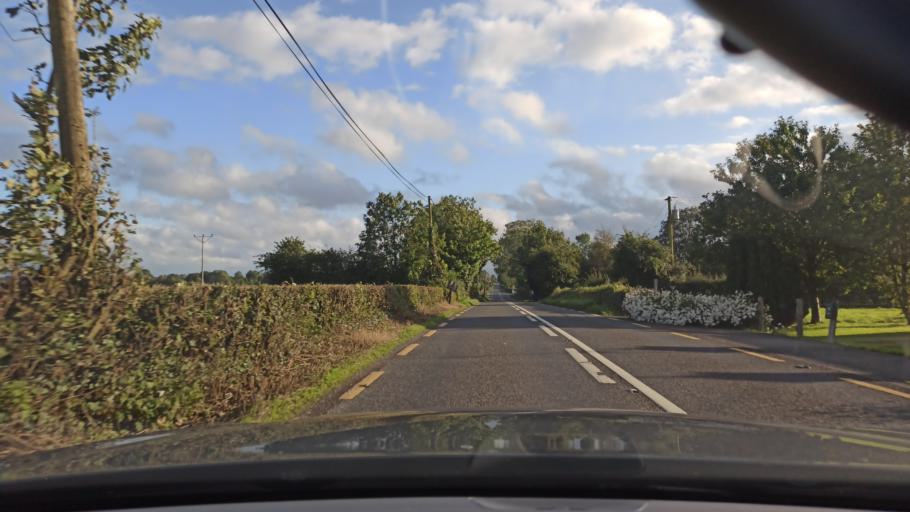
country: IE
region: Munster
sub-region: North Tipperary
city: Roscrea
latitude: 52.9024
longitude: -7.7970
